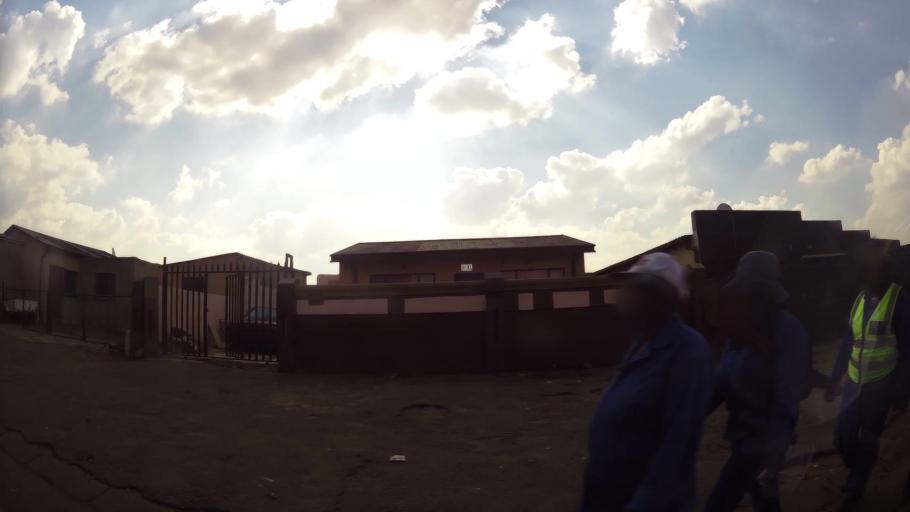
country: ZA
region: Gauteng
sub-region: Ekurhuleni Metropolitan Municipality
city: Germiston
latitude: -26.3519
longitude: 28.1485
